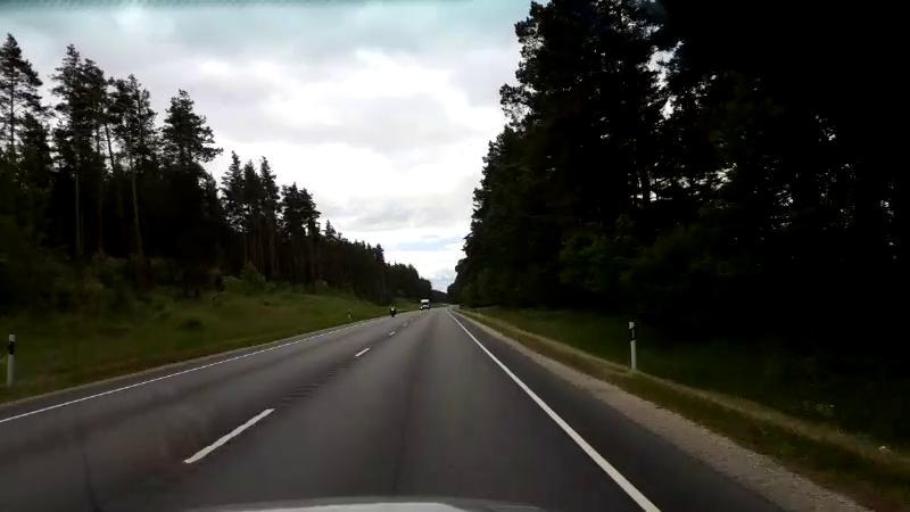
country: EE
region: Paernumaa
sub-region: Paernu linn
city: Parnu
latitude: 58.1688
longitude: 24.4958
